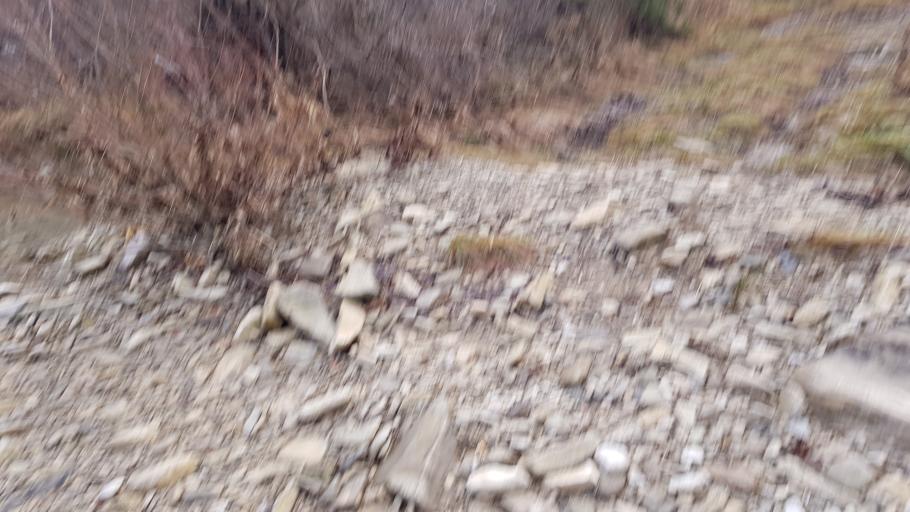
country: SI
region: Koper-Capodistria
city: Prade
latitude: 45.4667
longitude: 13.7811
